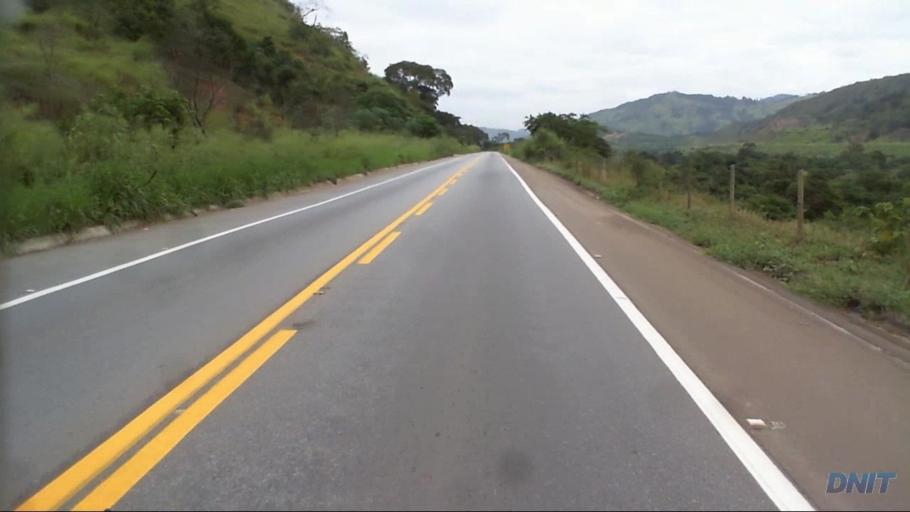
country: BR
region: Minas Gerais
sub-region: Timoteo
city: Timoteo
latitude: -19.5782
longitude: -42.7223
